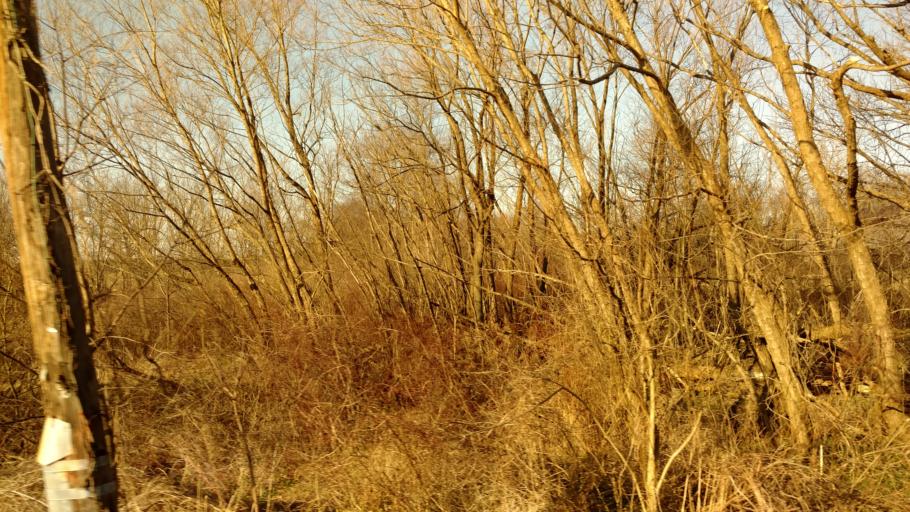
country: US
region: Ohio
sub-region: Crawford County
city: Galion
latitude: 40.7111
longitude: -82.7168
